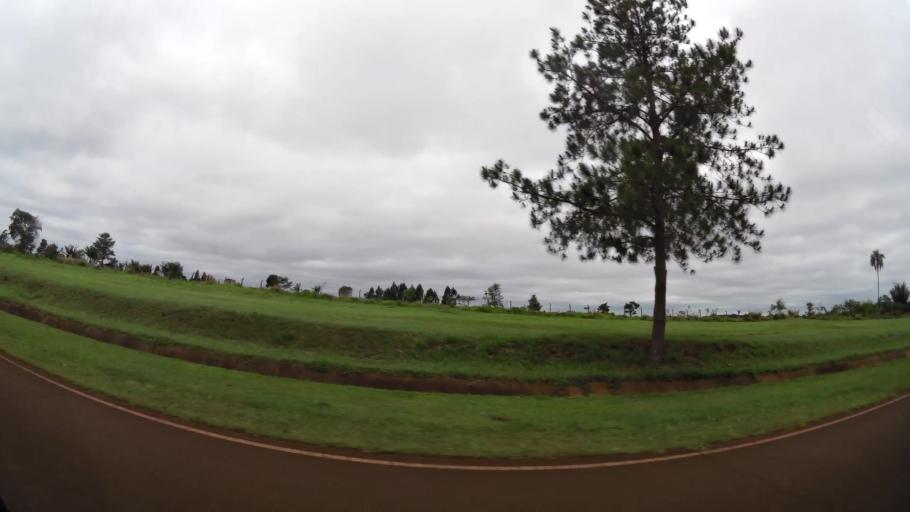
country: PY
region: Alto Parana
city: Colonia Yguazu
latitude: -25.4724
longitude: -54.8554
